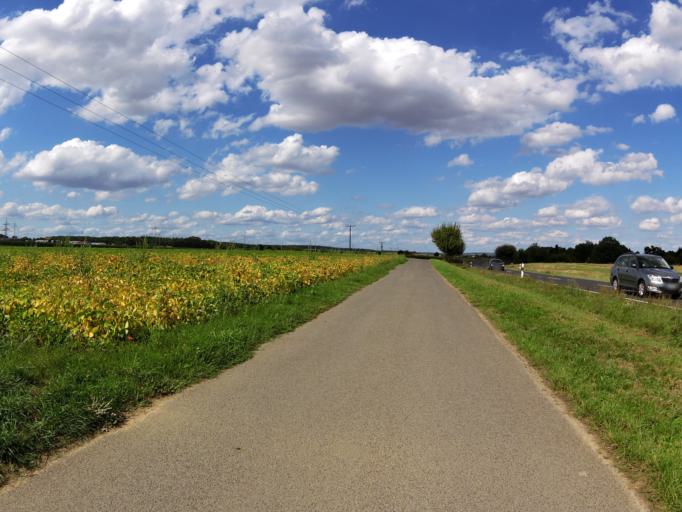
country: DE
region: Bavaria
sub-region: Regierungsbezirk Unterfranken
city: Bergrheinfeld
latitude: 49.9877
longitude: 10.1694
